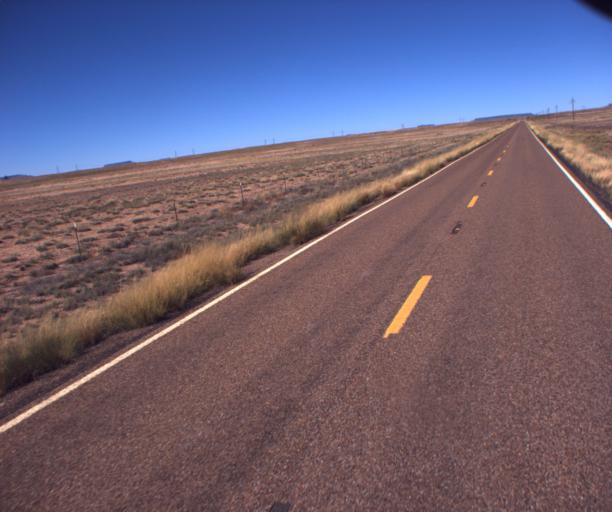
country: US
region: Arizona
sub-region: Navajo County
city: Holbrook
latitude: 35.1197
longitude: -110.0928
